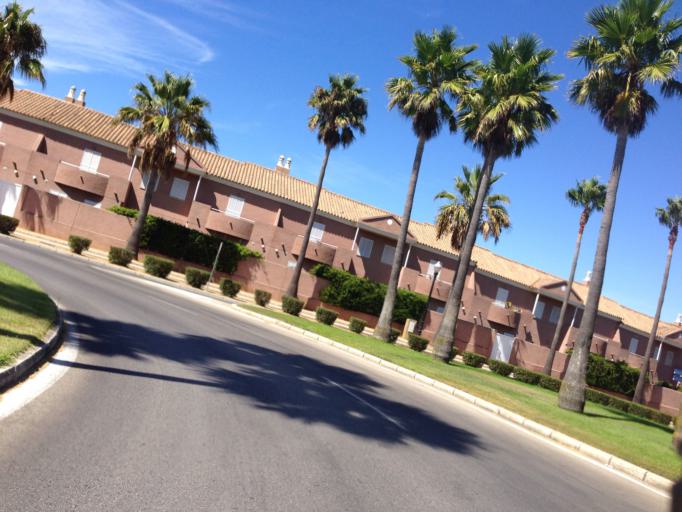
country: ES
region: Andalusia
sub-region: Provincia de Cadiz
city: Chiclana de la Frontera
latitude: 36.3443
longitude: -6.1536
